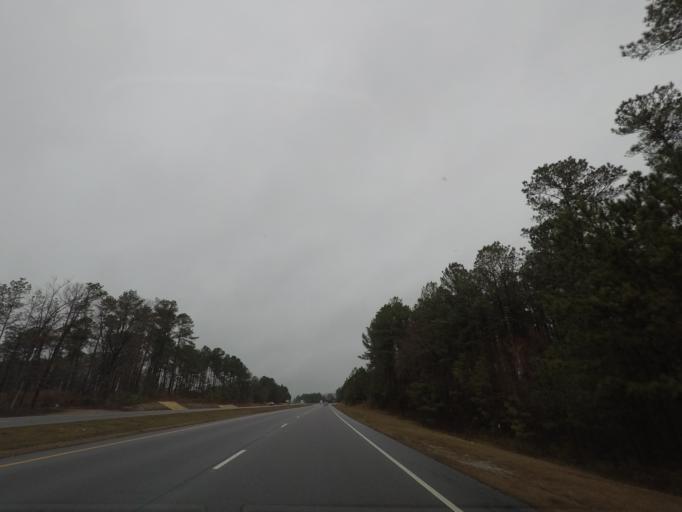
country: US
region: North Carolina
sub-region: Lee County
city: Broadway
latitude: 35.3290
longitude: -79.0938
